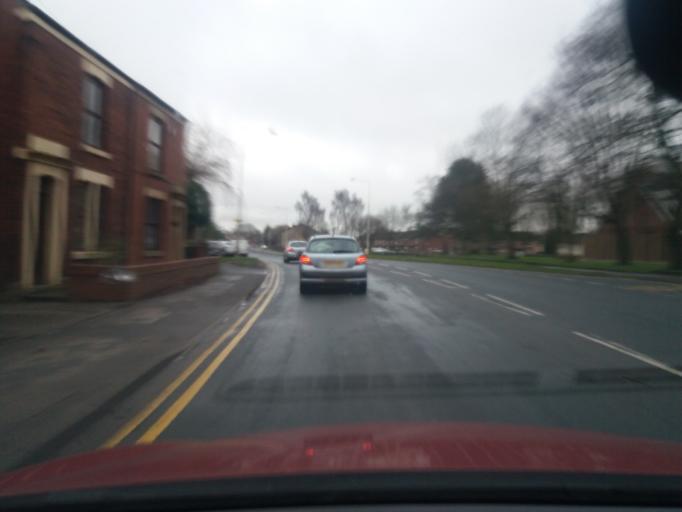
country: GB
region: England
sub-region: Lancashire
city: Clayton-le-Woods
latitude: 53.7054
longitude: -2.6398
